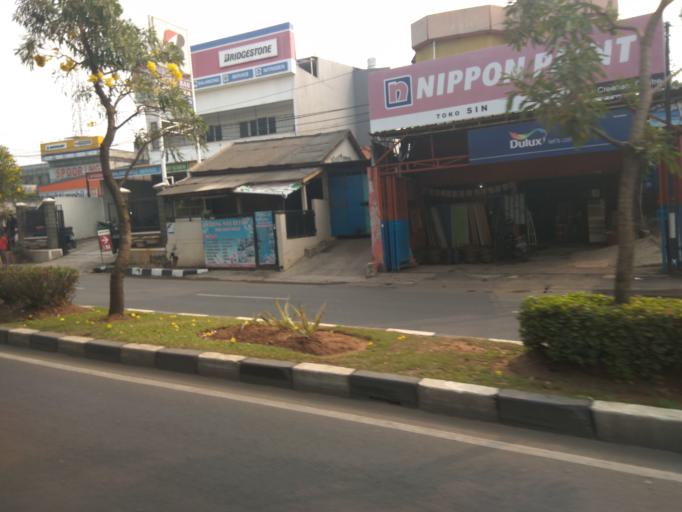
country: ID
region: West Java
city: Bekasi
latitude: -6.2614
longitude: 106.9980
